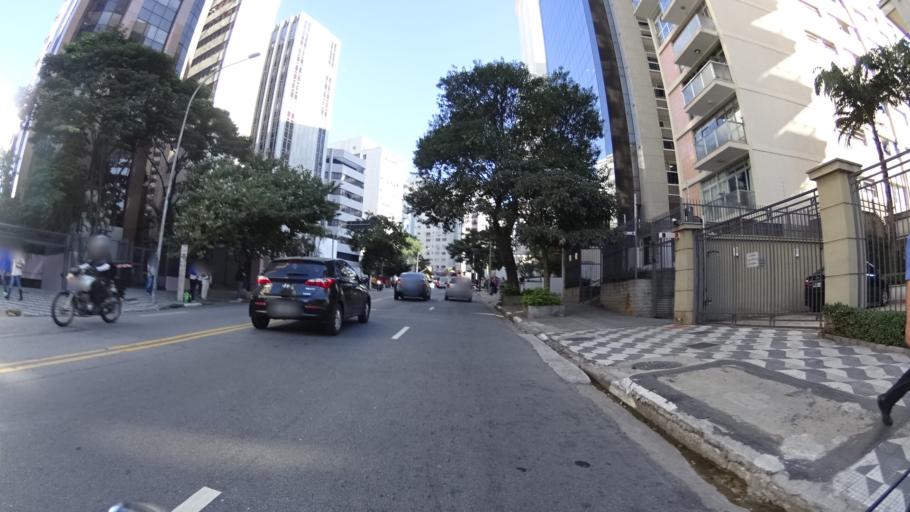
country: BR
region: Sao Paulo
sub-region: Sao Paulo
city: Sao Paulo
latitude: -23.5513
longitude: -46.6605
